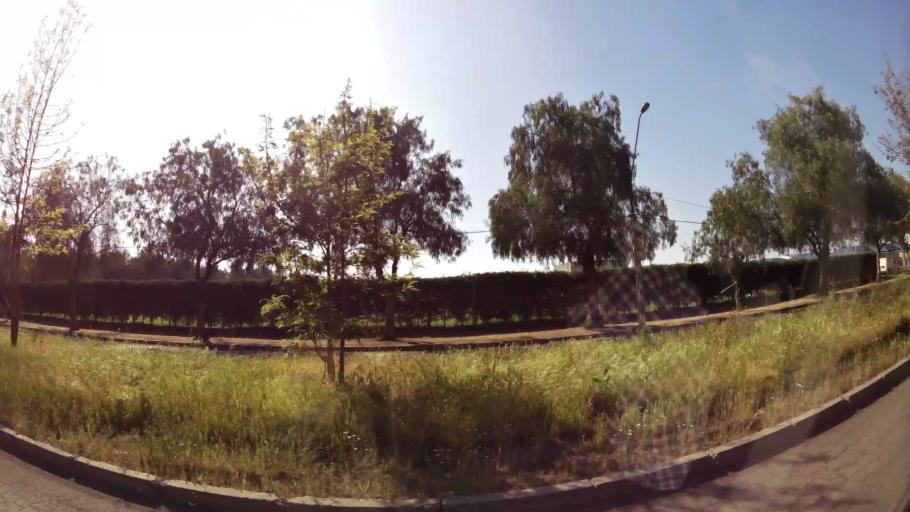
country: CL
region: Santiago Metropolitan
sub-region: Provincia de Chacabuco
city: Chicureo Abajo
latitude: -33.3315
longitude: -70.7198
